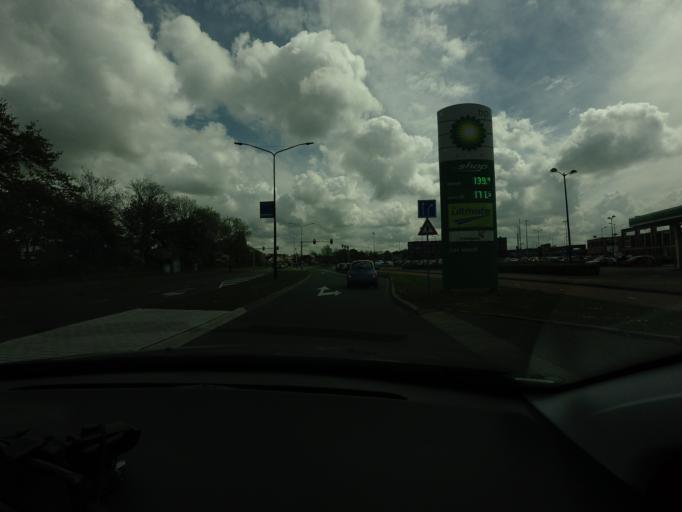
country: NL
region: North Holland
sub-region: Gemeente Heerhugowaard
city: Heerhugowaard
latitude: 52.6647
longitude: 4.8285
